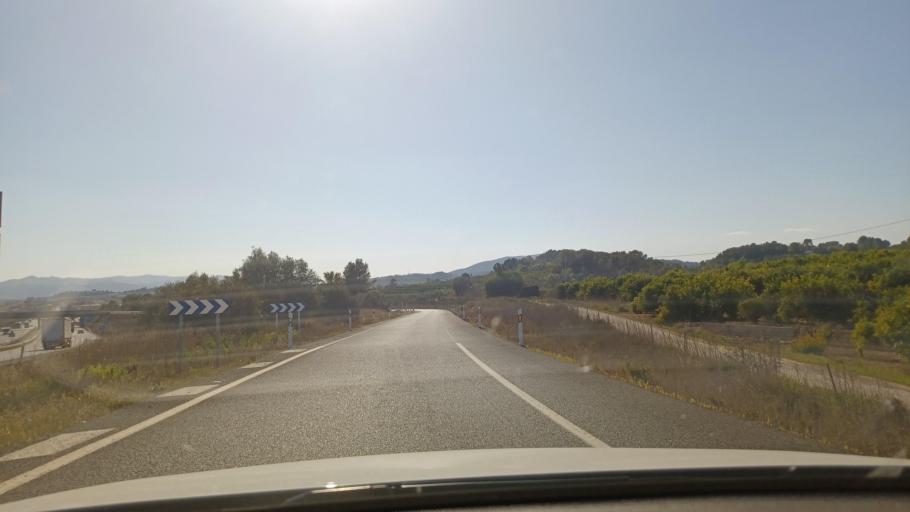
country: ES
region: Valencia
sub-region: Provincia de Valencia
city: Rotgla y Corbera
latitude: 39.0217
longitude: -0.5569
